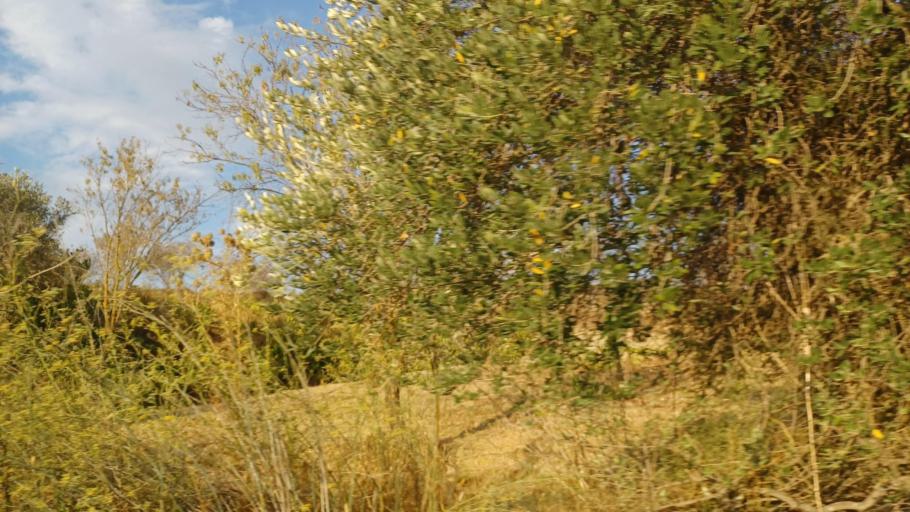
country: CY
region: Pafos
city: Tala
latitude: 34.9095
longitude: 32.5008
